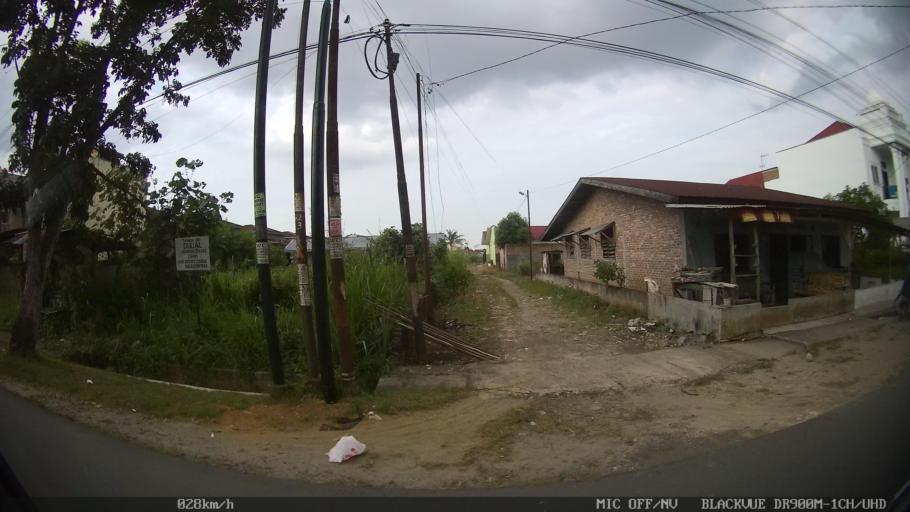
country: ID
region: North Sumatra
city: Sunggal
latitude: 3.5272
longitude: 98.6107
